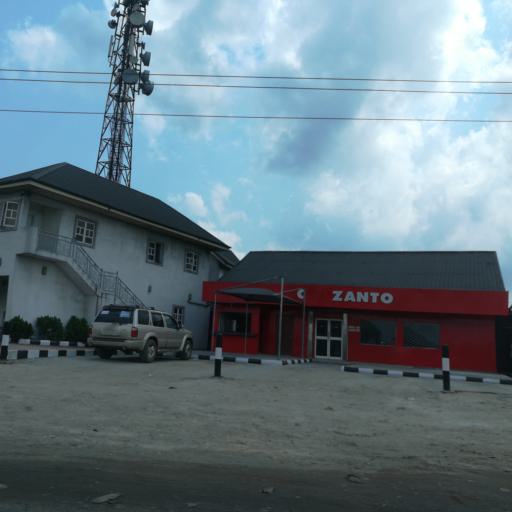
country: NG
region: Rivers
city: Okrika
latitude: 4.8238
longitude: 7.0921
